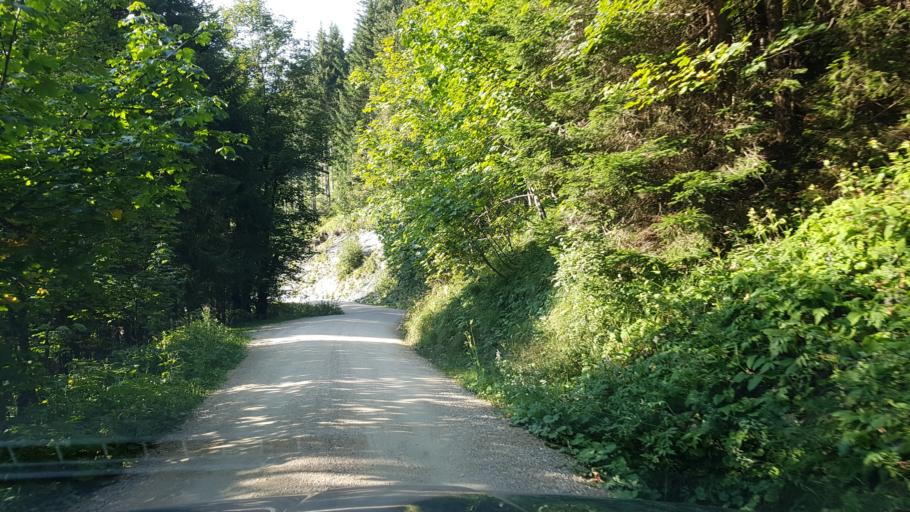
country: AT
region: Salzburg
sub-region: Politischer Bezirk Sankt Johann im Pongau
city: Kleinarl
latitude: 47.2740
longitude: 13.2485
